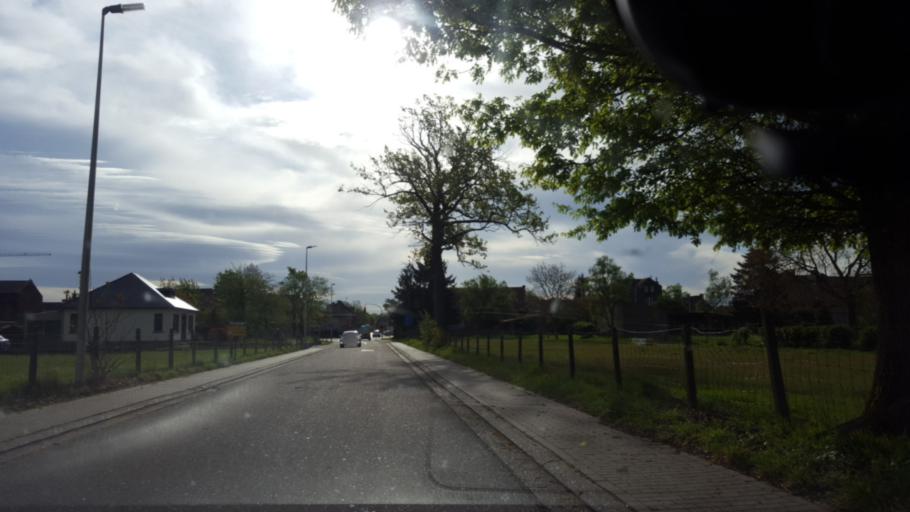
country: BE
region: Flanders
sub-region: Provincie Limburg
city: Lanaken
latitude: 50.9091
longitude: 5.6785
